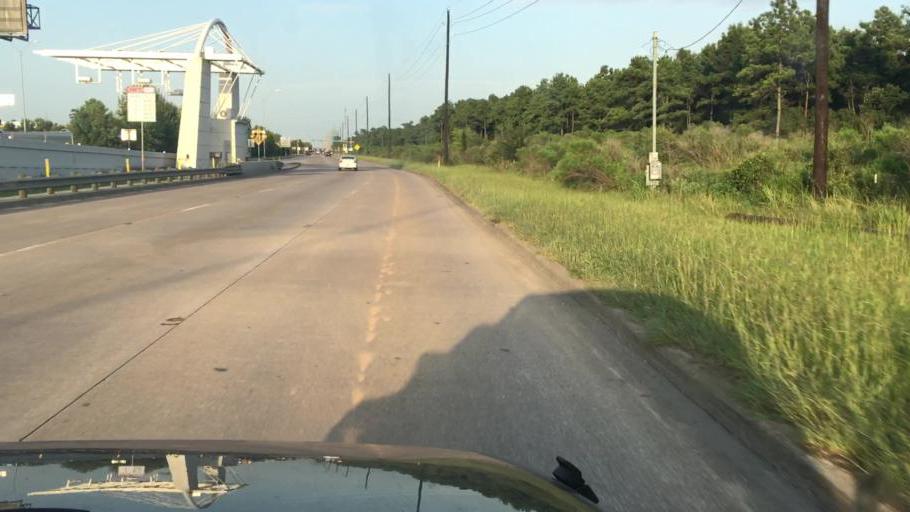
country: US
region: Texas
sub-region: Harris County
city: Humble
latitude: 29.9337
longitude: -95.2302
